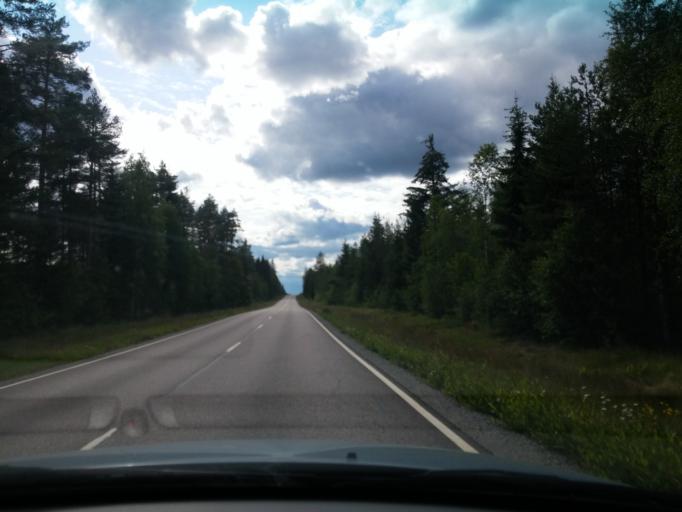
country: FI
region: Central Finland
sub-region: Saarijaervi-Viitasaari
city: Pylkoenmaeki
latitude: 62.6097
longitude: 24.6846
